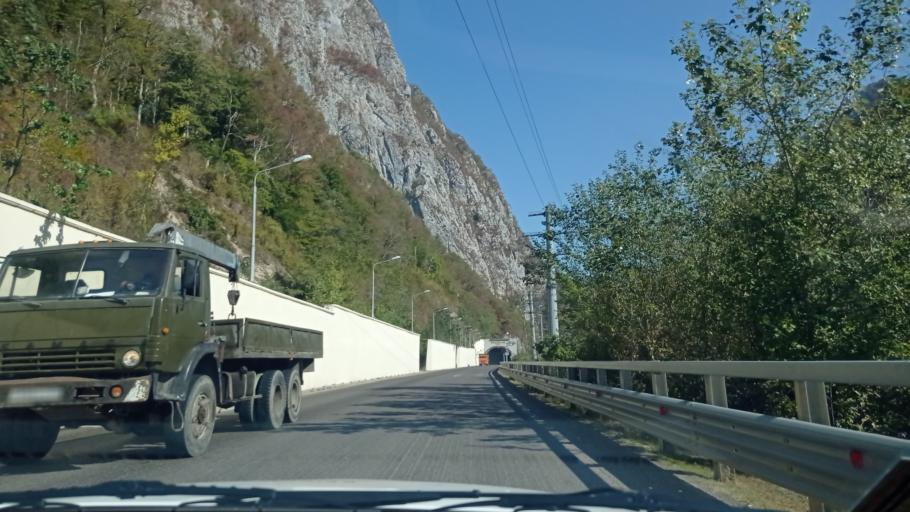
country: RU
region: Krasnodarskiy
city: Vysokoye
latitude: 43.5965
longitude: 40.0208
